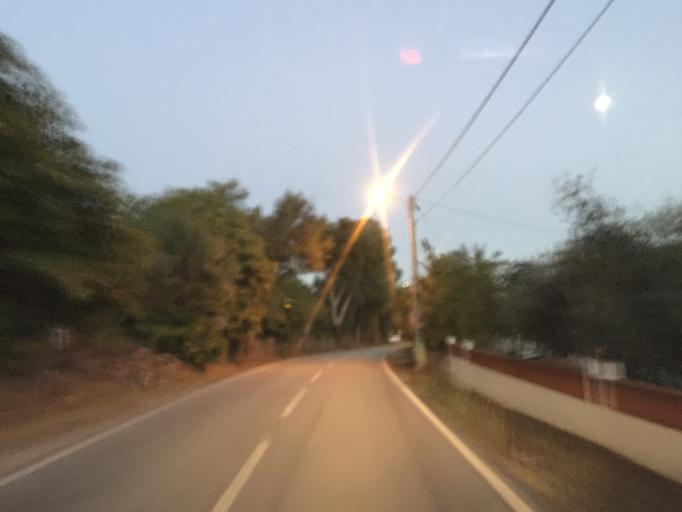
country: PT
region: Portalegre
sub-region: Castelo de Vide
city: Castelo de Vide
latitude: 39.3948
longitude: -7.4200
